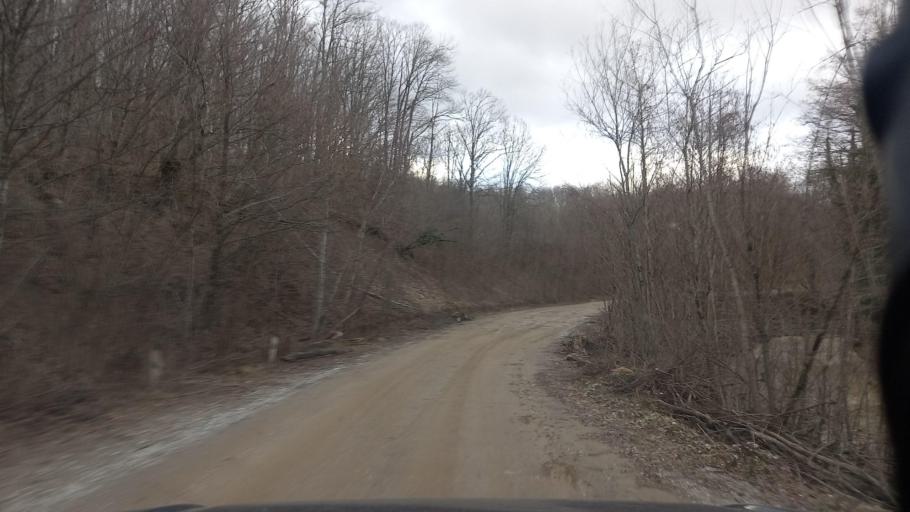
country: RU
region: Krasnodarskiy
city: Dzhubga
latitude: 44.4845
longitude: 38.7882
